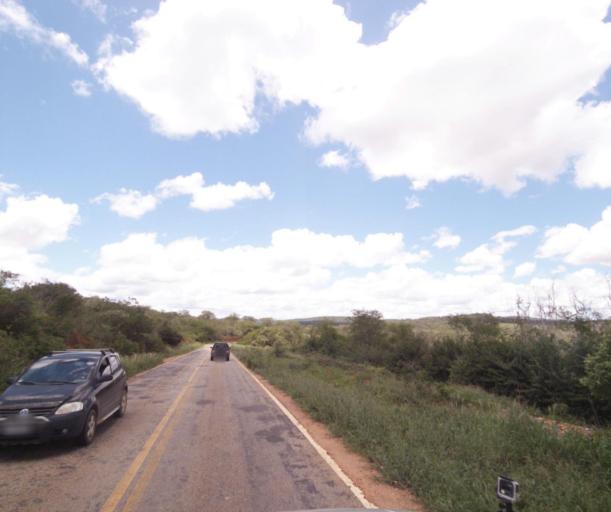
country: BR
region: Bahia
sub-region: Pocoes
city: Pocoes
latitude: -14.3877
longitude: -40.5197
